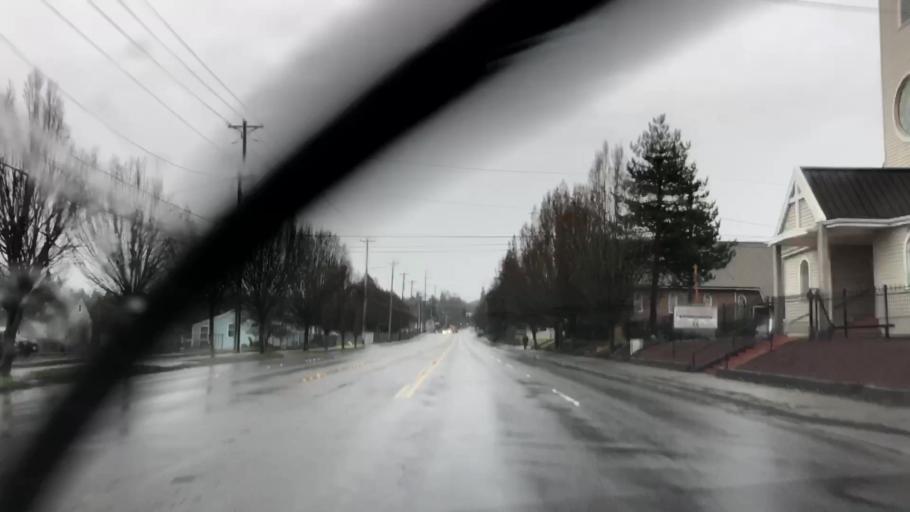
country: US
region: Washington
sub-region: Pierce County
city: Tacoma
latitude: 47.2333
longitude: -122.4093
